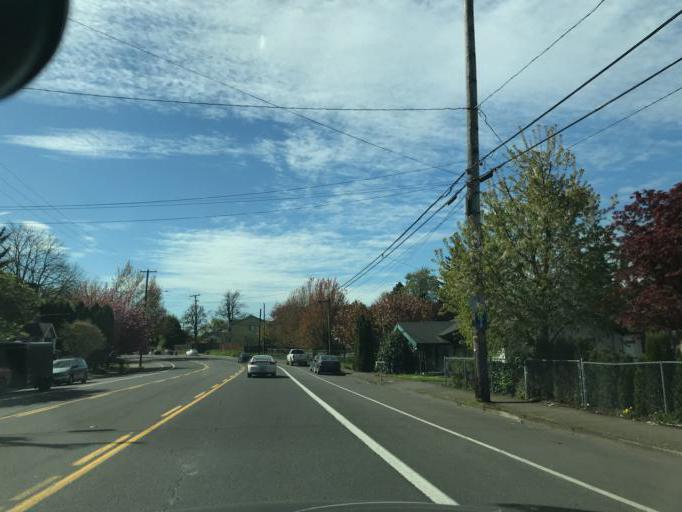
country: US
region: Oregon
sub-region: Multnomah County
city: Lents
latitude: 45.5037
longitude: -122.5687
